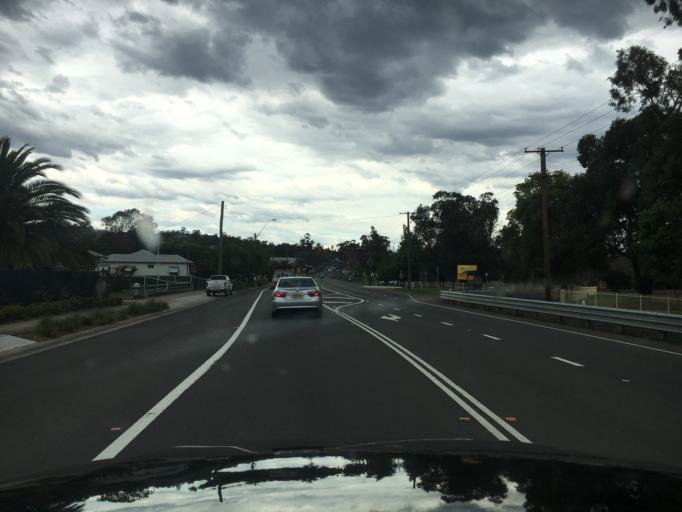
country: AU
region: New South Wales
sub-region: Muswellbrook
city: Muswellbrook
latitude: -32.1592
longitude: 150.8868
